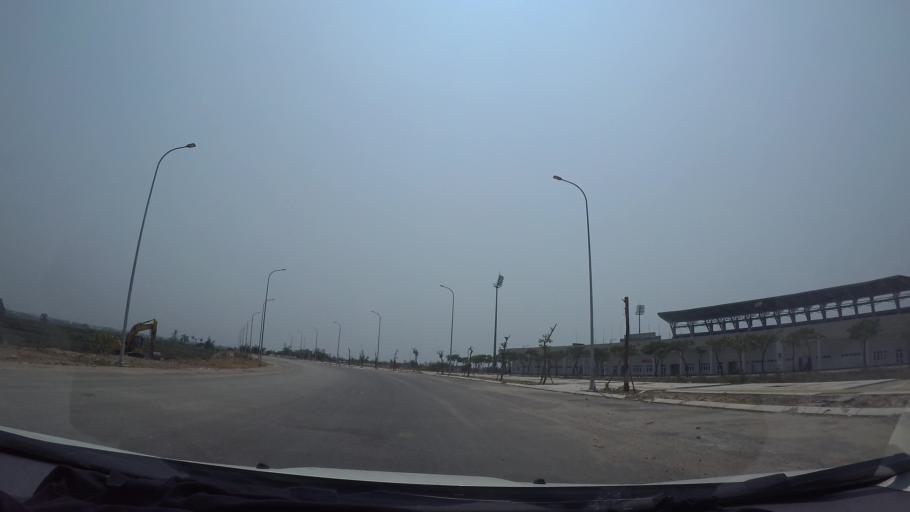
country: VN
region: Da Nang
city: Cam Le
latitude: 16.0001
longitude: 108.2248
